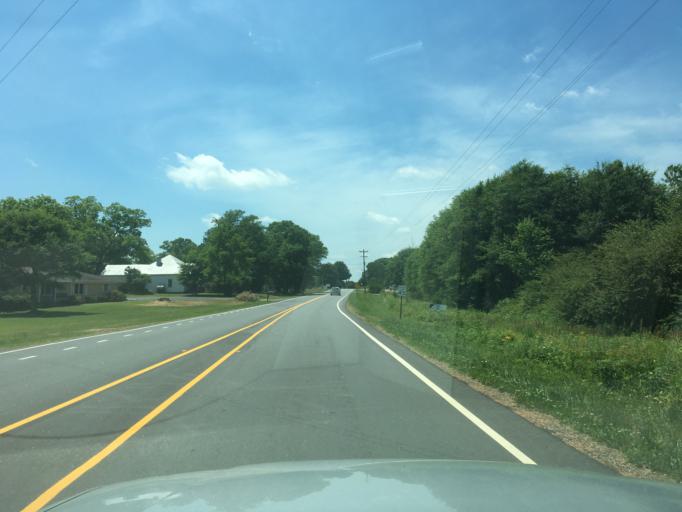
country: US
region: Georgia
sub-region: Hart County
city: Reed Creek
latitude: 34.5093
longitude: -82.9694
